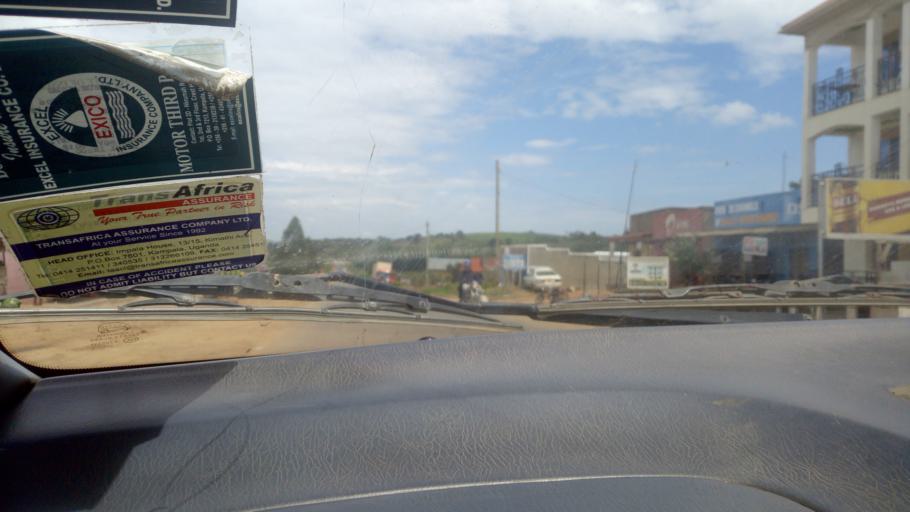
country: UG
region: Western Region
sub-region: Mbarara District
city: Bwizibwera
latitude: -0.4073
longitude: 30.5686
